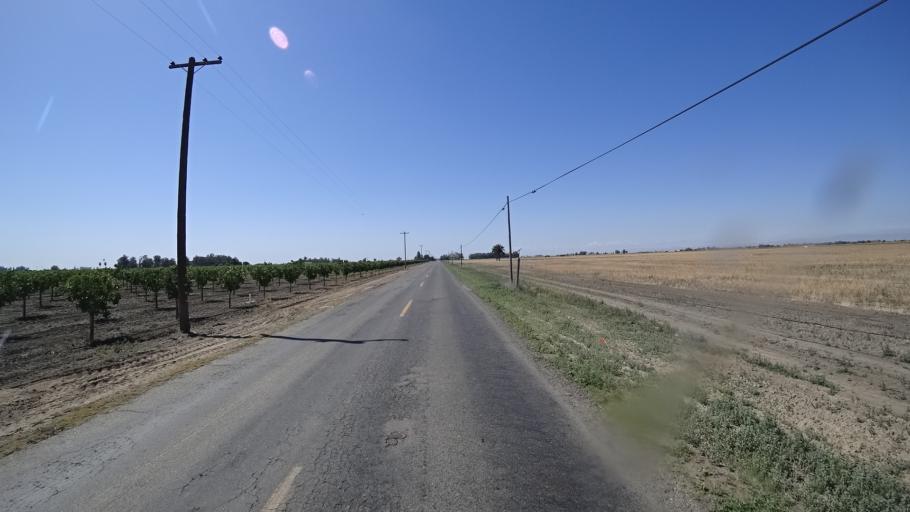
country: US
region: California
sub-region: Kings County
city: Stratford
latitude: 36.2097
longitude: -119.7982
